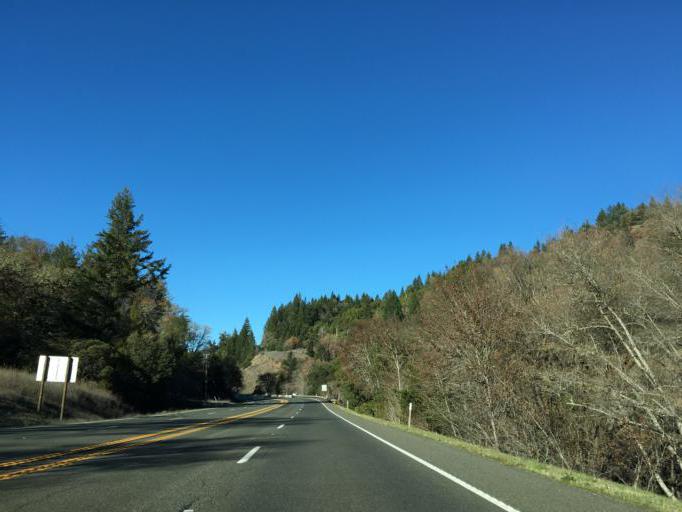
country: US
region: California
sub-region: Mendocino County
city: Brooktrails
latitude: 39.5609
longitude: -123.4329
